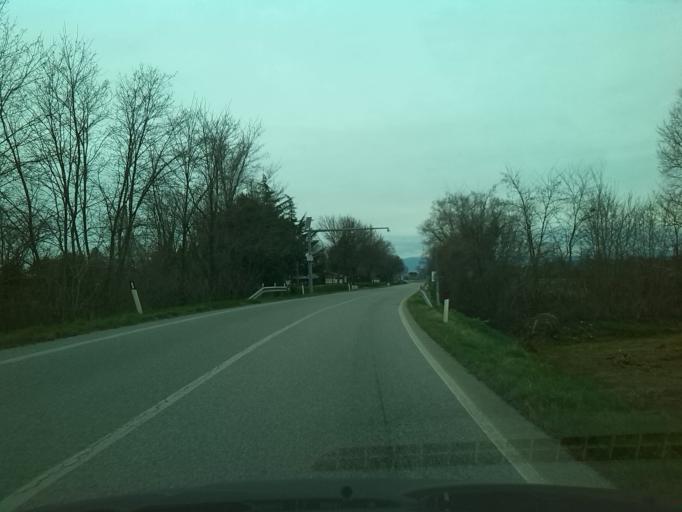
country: IT
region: Friuli Venezia Giulia
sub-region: Provincia di Gorizia
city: Mariano del Friuli
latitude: 45.9250
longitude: 13.4535
